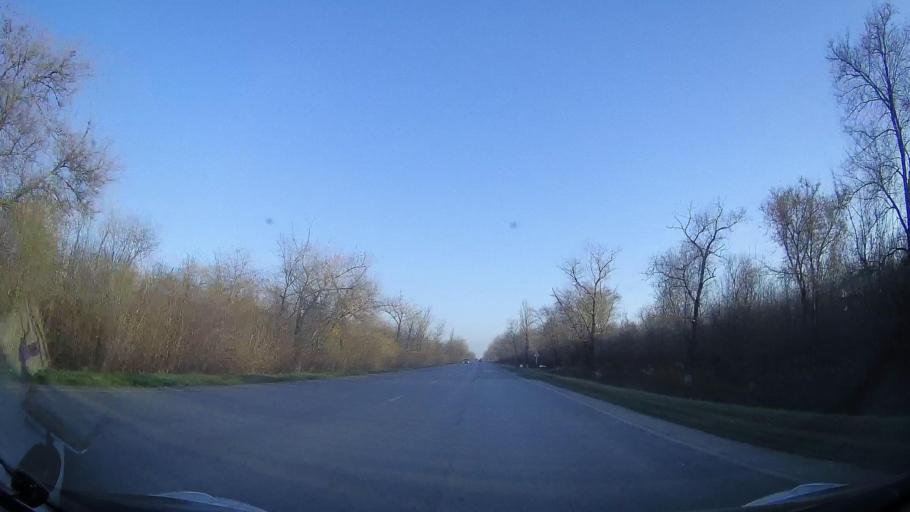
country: RU
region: Rostov
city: Bataysk
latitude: 47.0439
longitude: 39.8513
